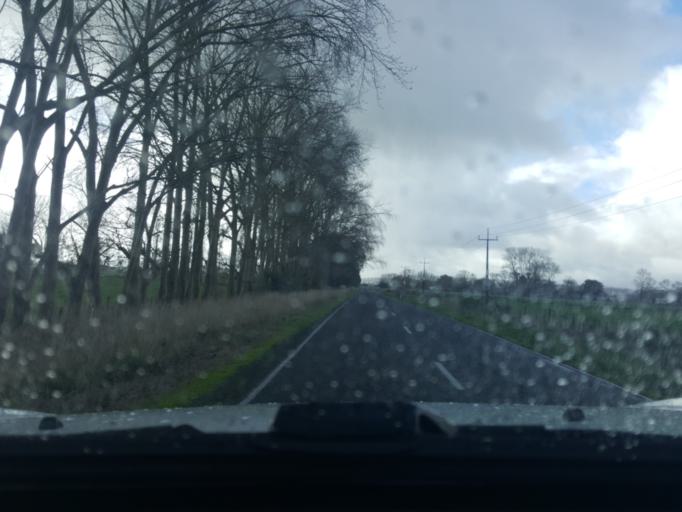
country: NZ
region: Waikato
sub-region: Waikato District
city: Te Kauwhata
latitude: -37.4468
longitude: 175.1108
